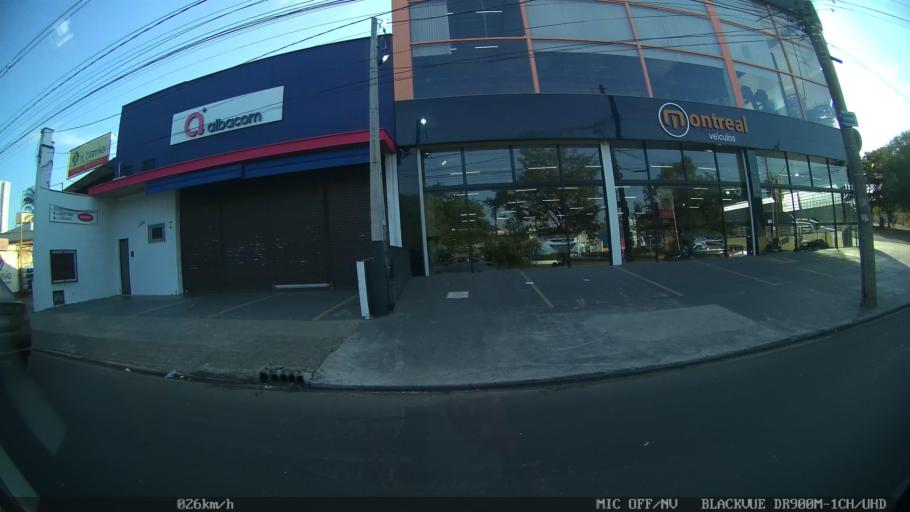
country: BR
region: Sao Paulo
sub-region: Piracicaba
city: Piracicaba
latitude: -22.7454
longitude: -47.6446
